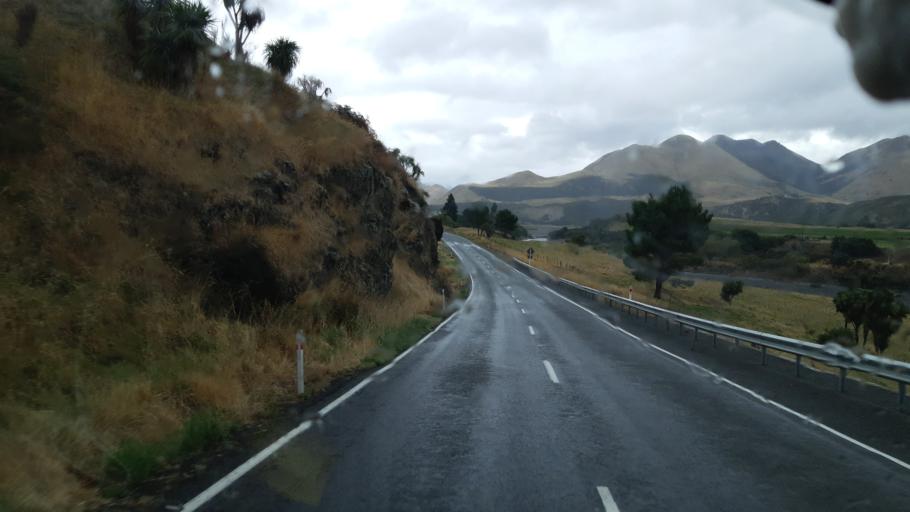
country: NZ
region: Canterbury
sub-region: Hurunui District
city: Amberley
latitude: -42.6367
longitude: 172.7721
